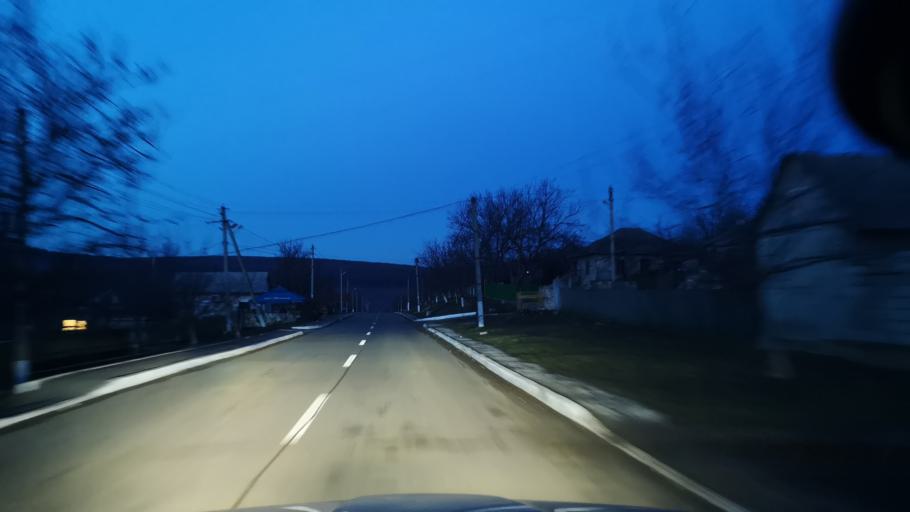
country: MD
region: Orhei
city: Orhei
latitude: 47.3351
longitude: 28.6565
